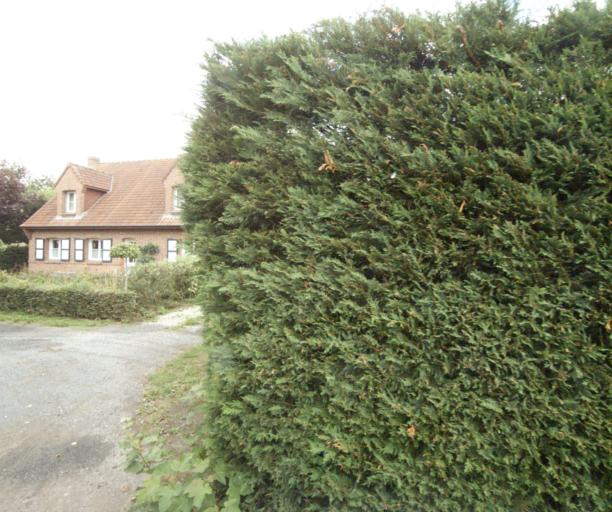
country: FR
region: Nord-Pas-de-Calais
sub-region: Departement du Nord
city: Anstaing
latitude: 50.5825
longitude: 3.1895
